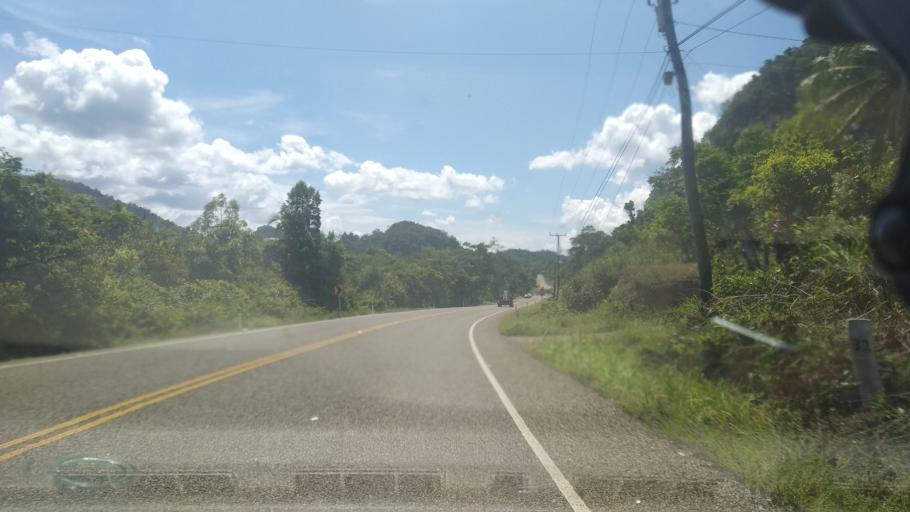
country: BZ
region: Cayo
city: Belmopan
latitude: 17.0883
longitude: -88.6168
